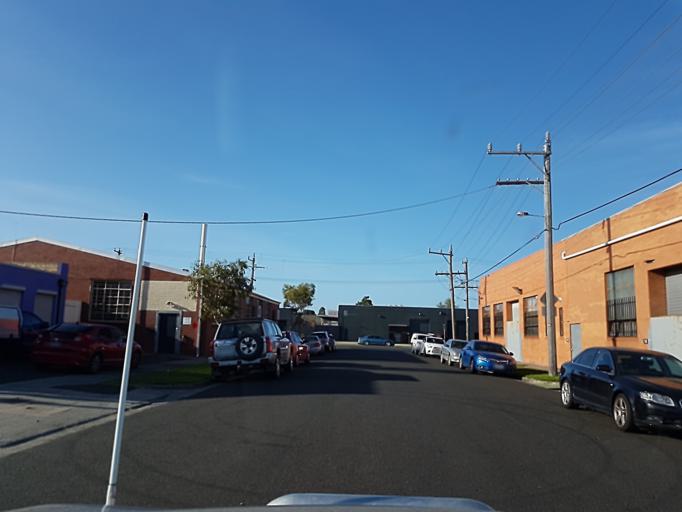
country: AU
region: Victoria
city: Highett
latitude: -37.9423
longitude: 145.0686
